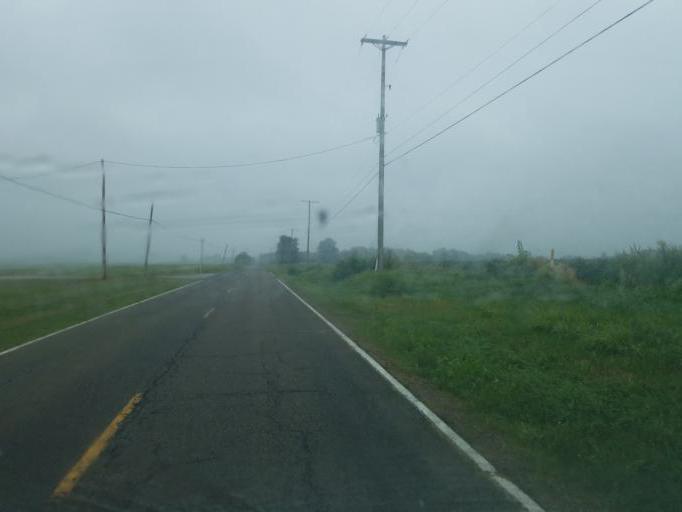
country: US
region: Ohio
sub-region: Licking County
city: Johnstown
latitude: 40.2249
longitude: -82.6935
